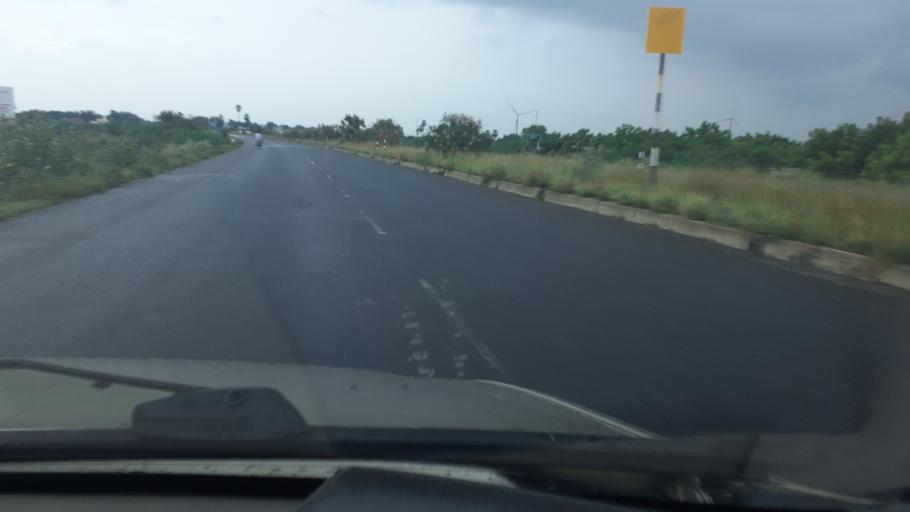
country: IN
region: Tamil Nadu
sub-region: Thoothukkudi
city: Kadambur
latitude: 9.0428
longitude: 77.7925
